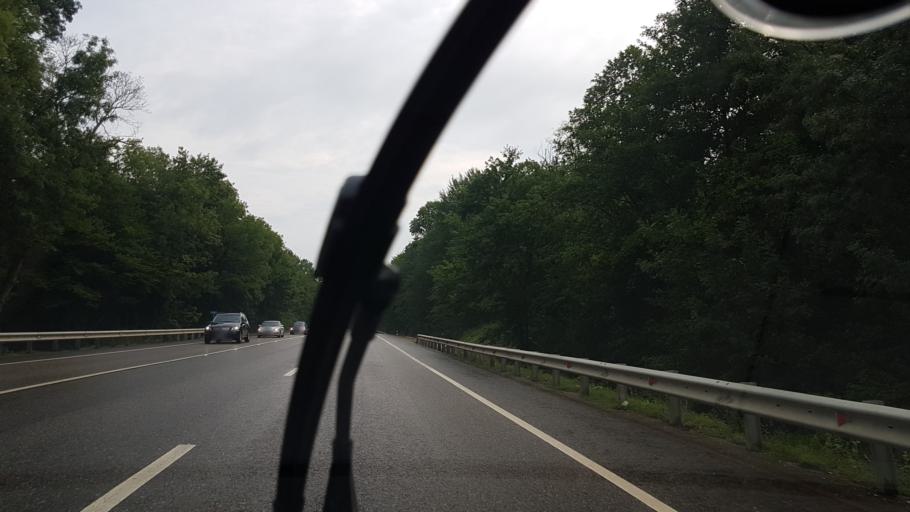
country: RU
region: Krasnodarskiy
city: Dzhubga
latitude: 44.4088
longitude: 38.7381
